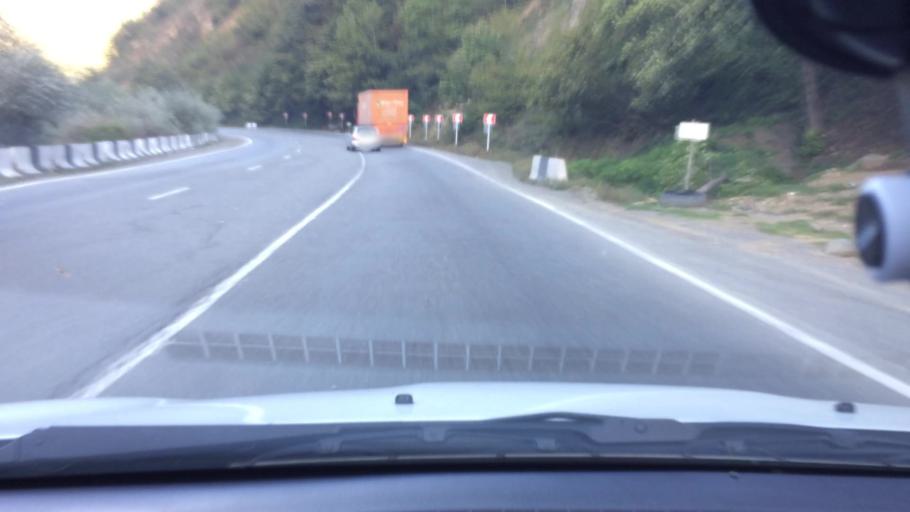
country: GE
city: Surami
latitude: 42.0937
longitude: 43.4603
